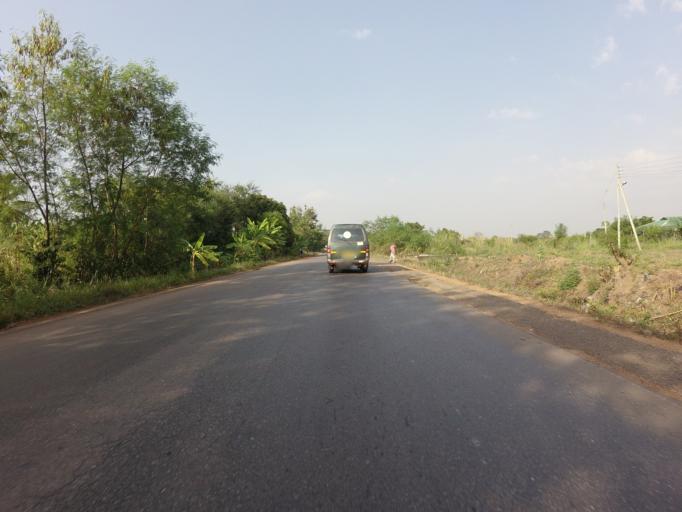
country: GH
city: Akropong
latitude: 6.1865
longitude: 0.0740
